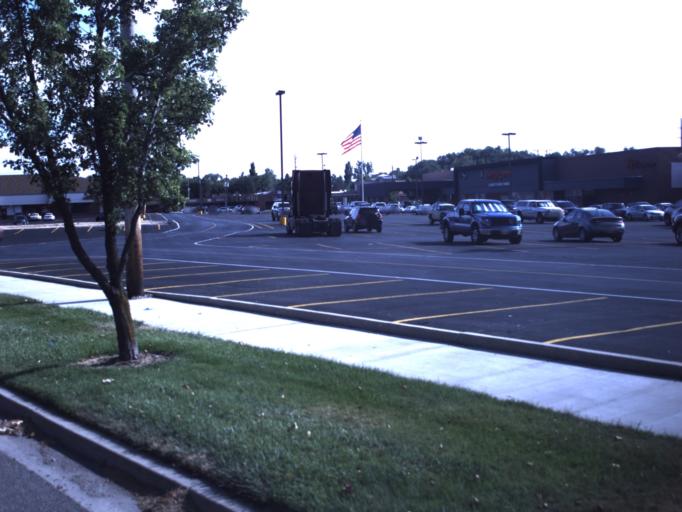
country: US
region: Utah
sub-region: Weber County
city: Harrisville
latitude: 41.2614
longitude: -111.9713
